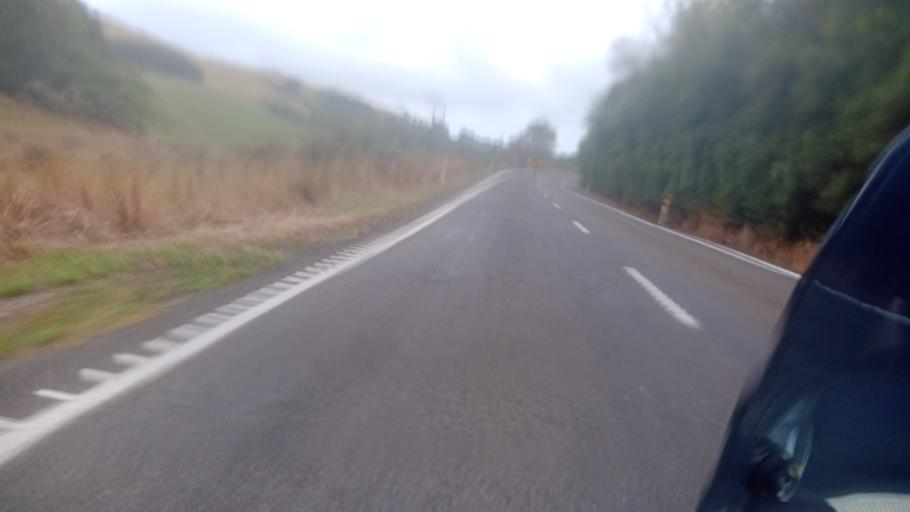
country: NZ
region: Bay of Plenty
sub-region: Opotiki District
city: Opotiki
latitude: -38.4000
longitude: 177.5609
